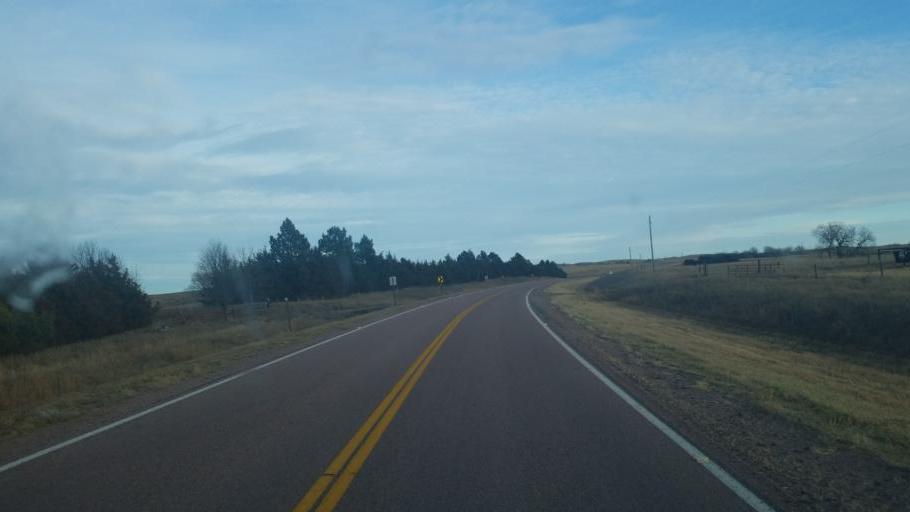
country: US
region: South Dakota
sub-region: Bon Homme County
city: Springfield
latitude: 42.7331
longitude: -97.8824
